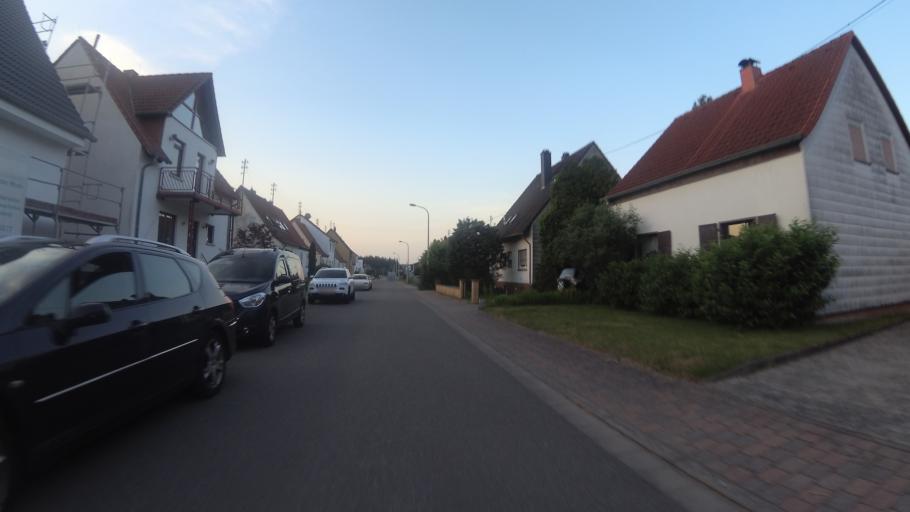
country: DE
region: Rheinland-Pfalz
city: Bruchmuhlbach-Miesau
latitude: 49.4012
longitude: 7.4258
